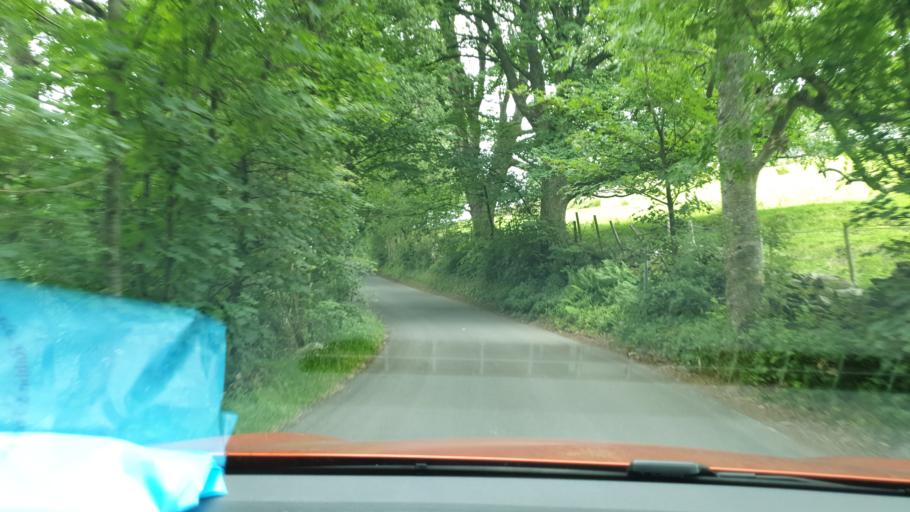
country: GB
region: England
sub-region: Cumbria
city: Penrith
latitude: 54.5714
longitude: -2.8610
